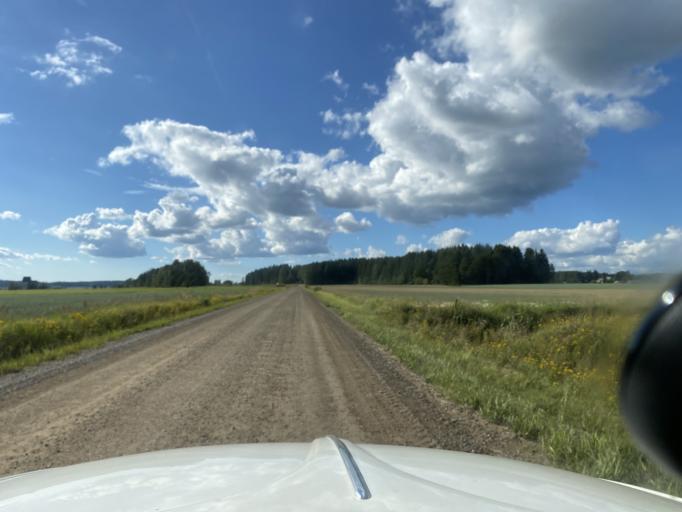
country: FI
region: Pirkanmaa
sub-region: Lounais-Pirkanmaa
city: Punkalaidun
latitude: 61.1355
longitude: 23.2253
